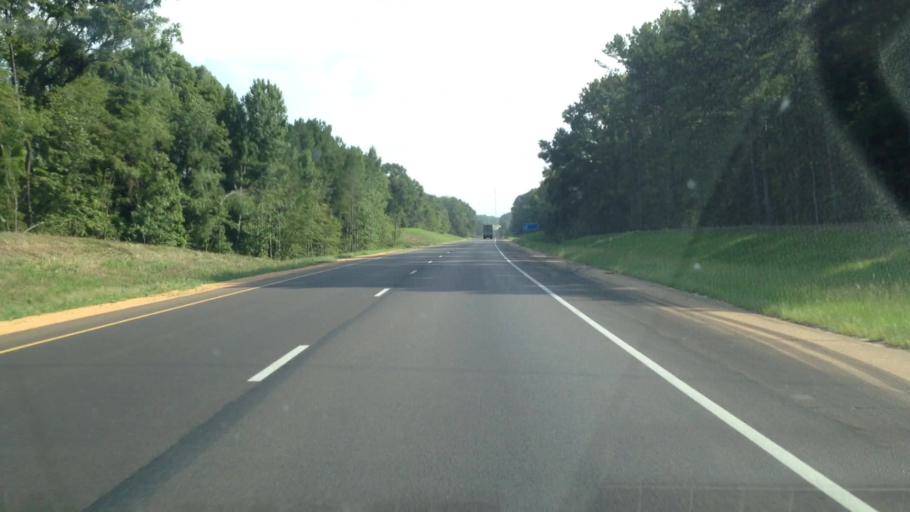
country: US
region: Mississippi
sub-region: Copiah County
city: Crystal Springs
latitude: 31.9974
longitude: -90.3694
